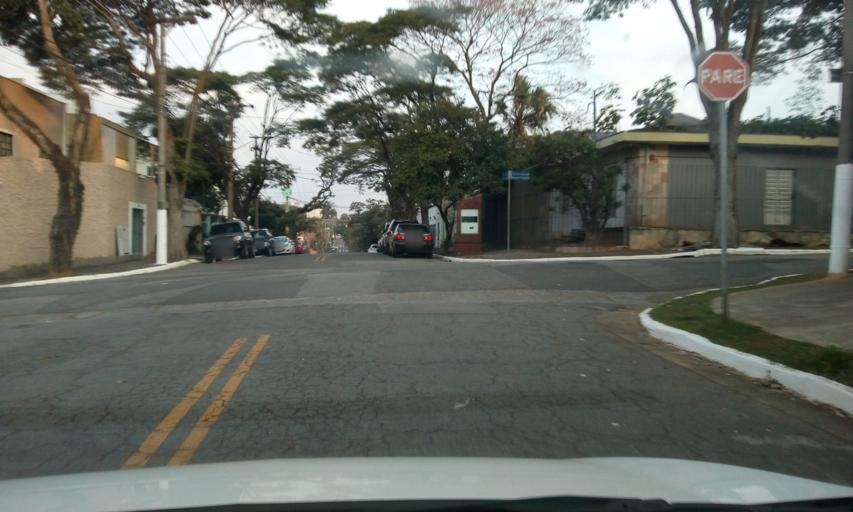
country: BR
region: Sao Paulo
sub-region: Sao Paulo
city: Sao Paulo
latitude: -23.6133
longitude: -46.6467
